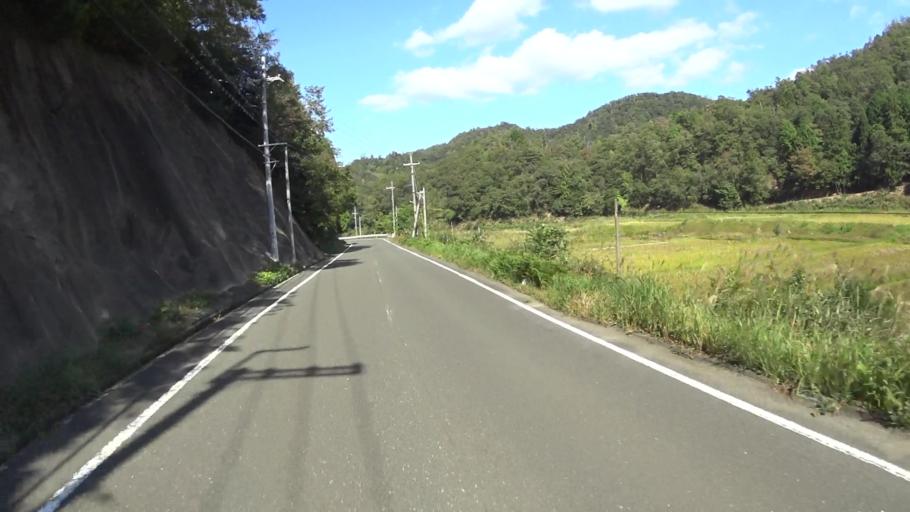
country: JP
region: Hyogo
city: Toyooka
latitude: 35.5578
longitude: 134.9793
